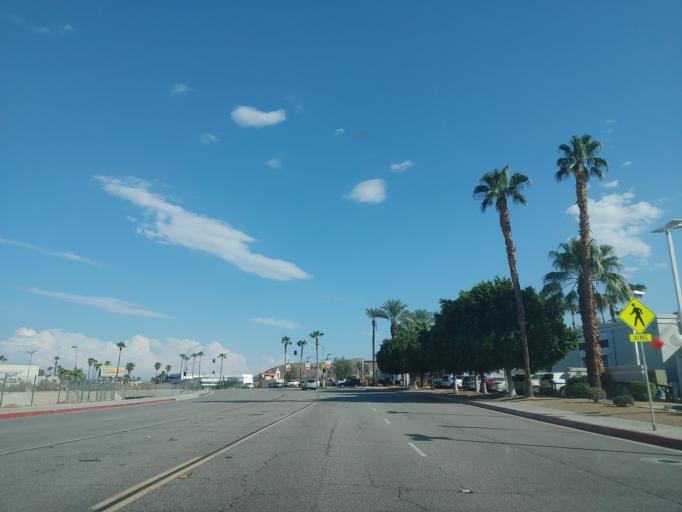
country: US
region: California
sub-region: Riverside County
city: Cathedral City
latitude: 33.7857
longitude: -116.4719
